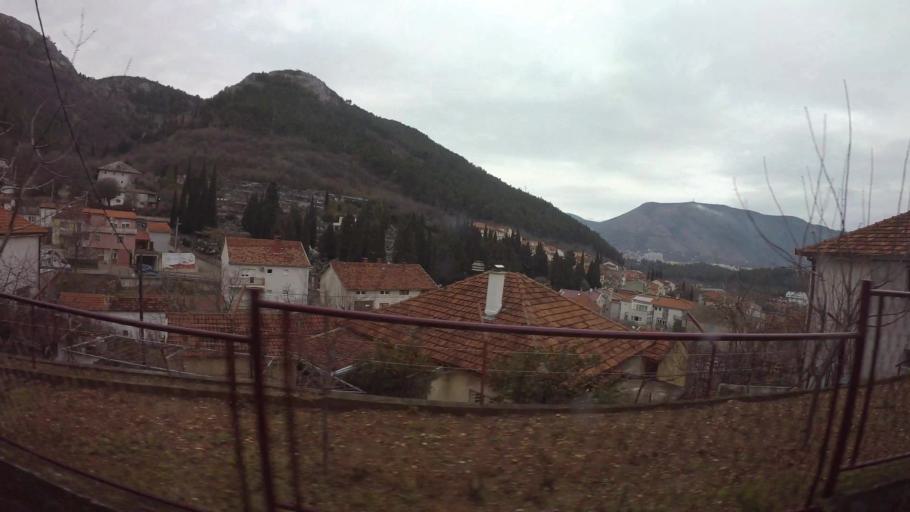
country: BA
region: Federation of Bosnia and Herzegovina
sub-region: Hercegovacko-Bosanski Kanton
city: Mostar
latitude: 43.3320
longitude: 17.7971
